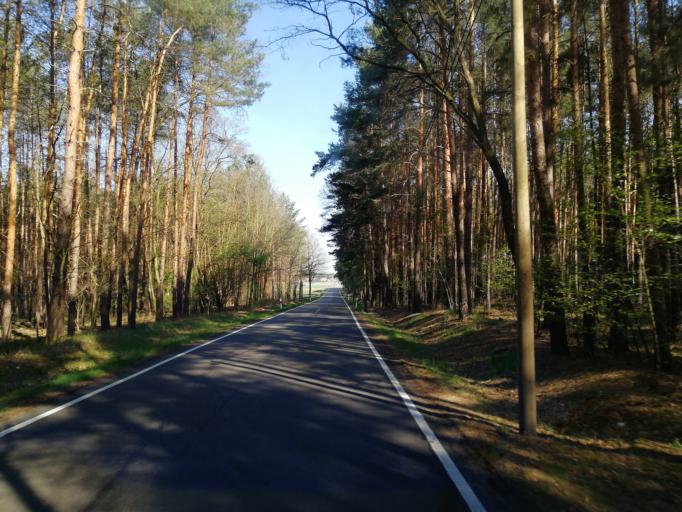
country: DE
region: Brandenburg
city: Bronkow
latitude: 51.7257
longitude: 13.8564
